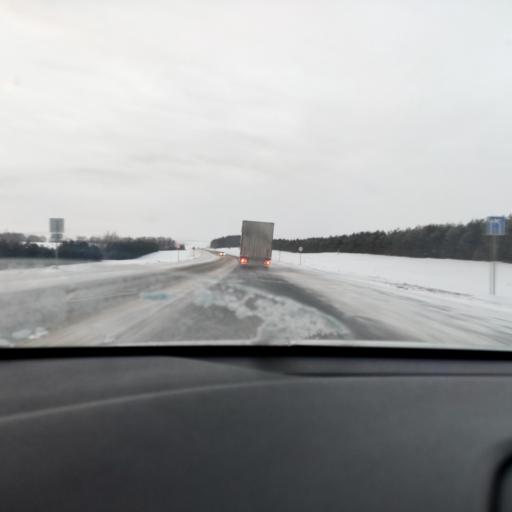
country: RU
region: Tatarstan
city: Sviyazhsk
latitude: 55.6360
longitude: 48.7868
